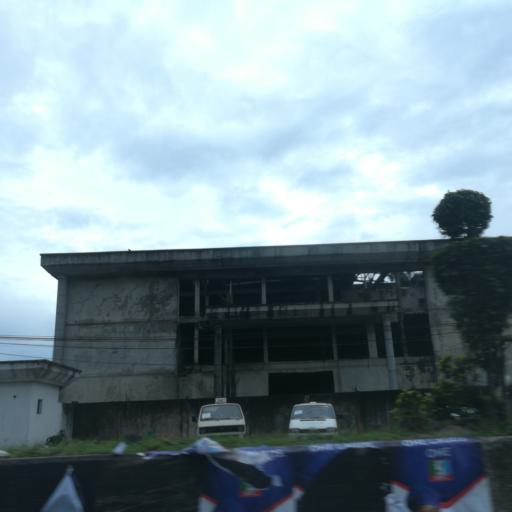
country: NG
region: Lagos
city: Makoko
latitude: 6.5046
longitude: 3.3778
